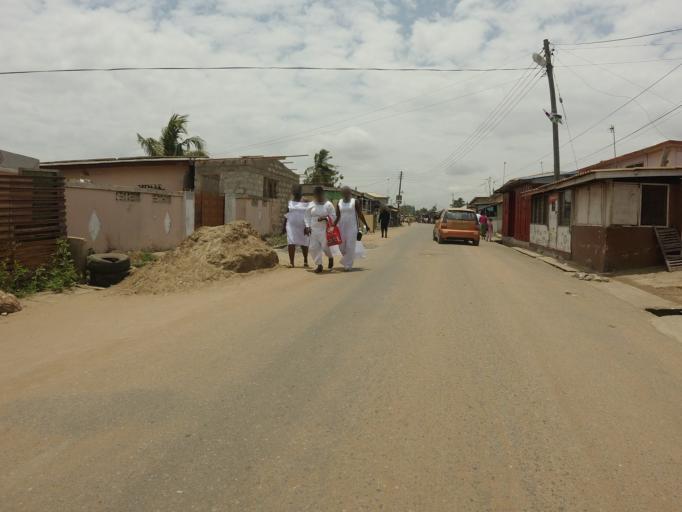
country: GH
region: Greater Accra
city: Nungua
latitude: 5.5995
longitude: -0.0827
